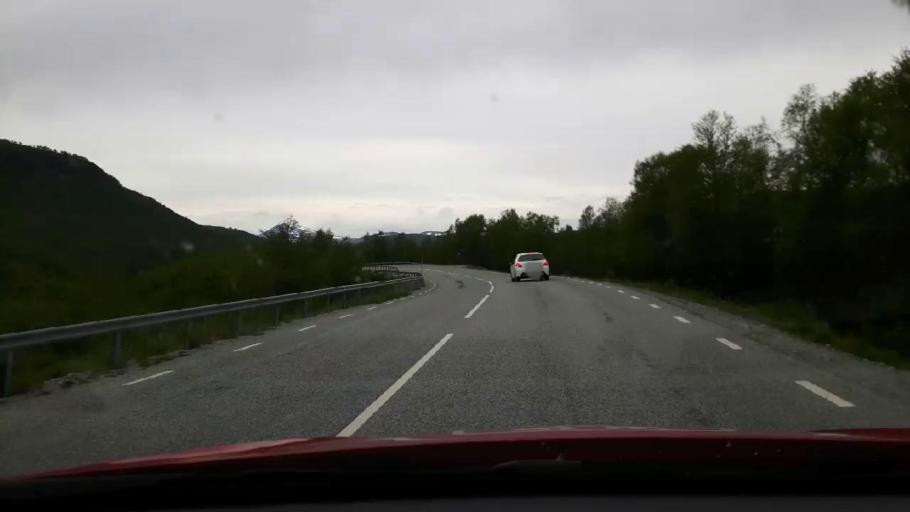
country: NO
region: Sor-Trondelag
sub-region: Tydal
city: Aas
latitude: 62.6814
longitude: 12.4170
